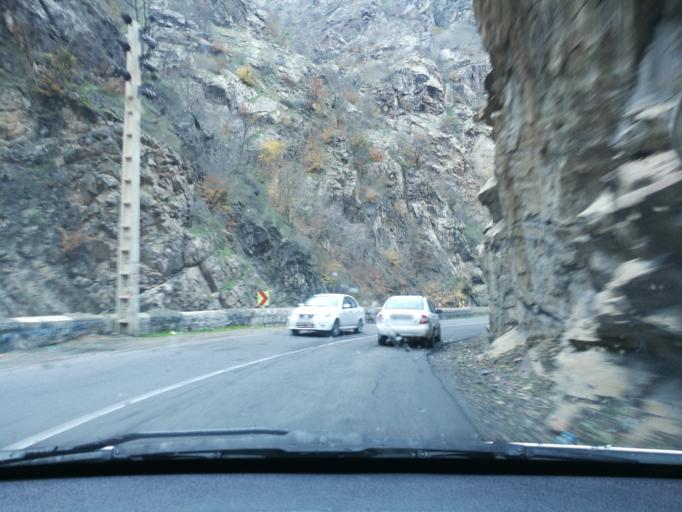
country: IR
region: Mazandaran
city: Chalus
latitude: 36.2892
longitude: 51.2402
